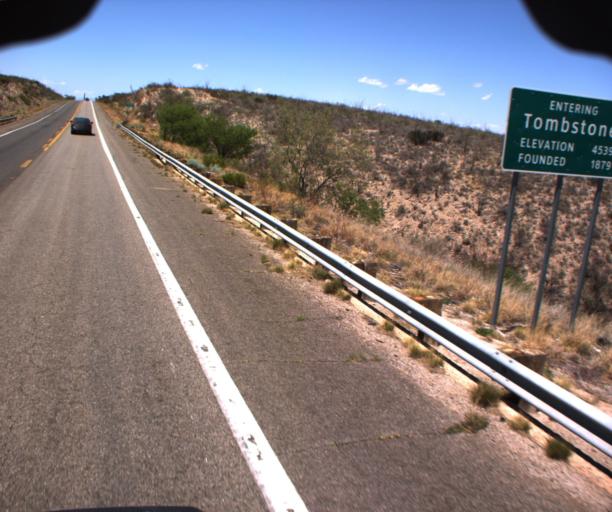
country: US
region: Arizona
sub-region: Cochise County
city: Tombstone
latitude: 31.7036
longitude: -110.0504
